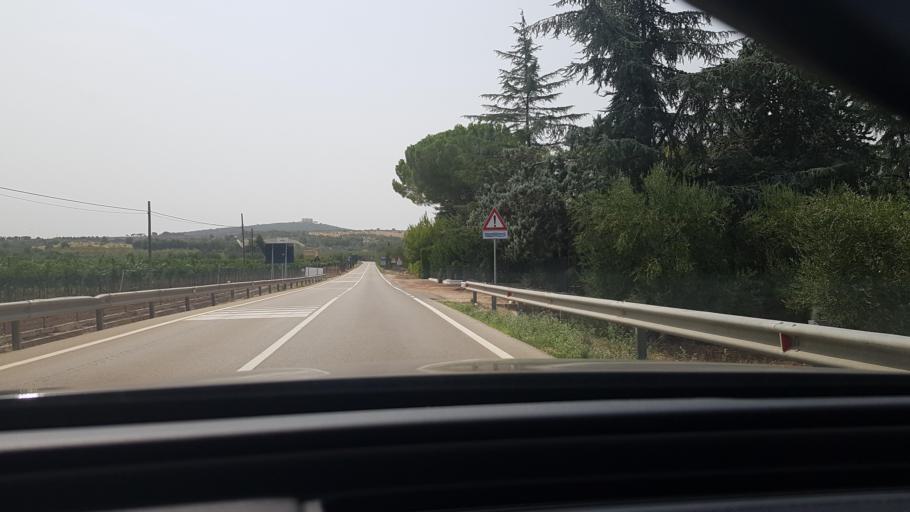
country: IT
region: Apulia
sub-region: Provincia di Barletta - Andria - Trani
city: Andria
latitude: 41.1170
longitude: 16.2829
